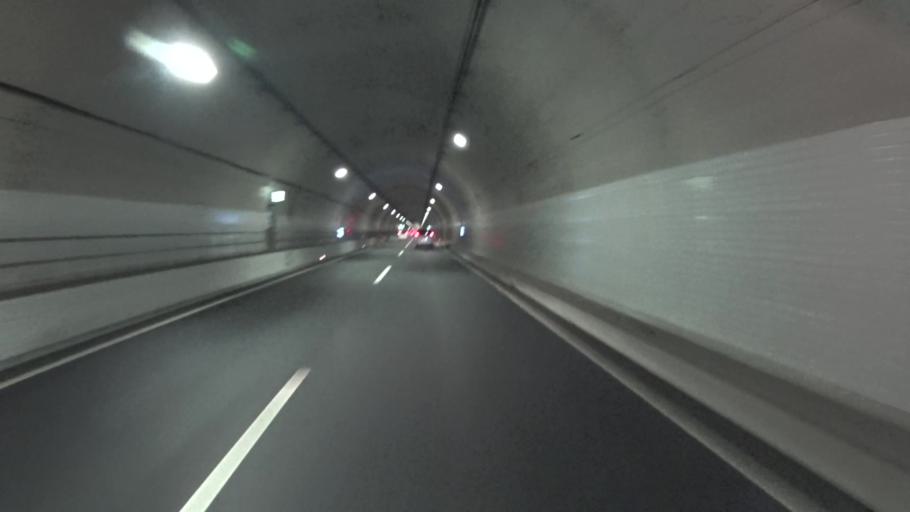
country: JP
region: Kyoto
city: Muko
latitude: 34.9329
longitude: 135.6647
